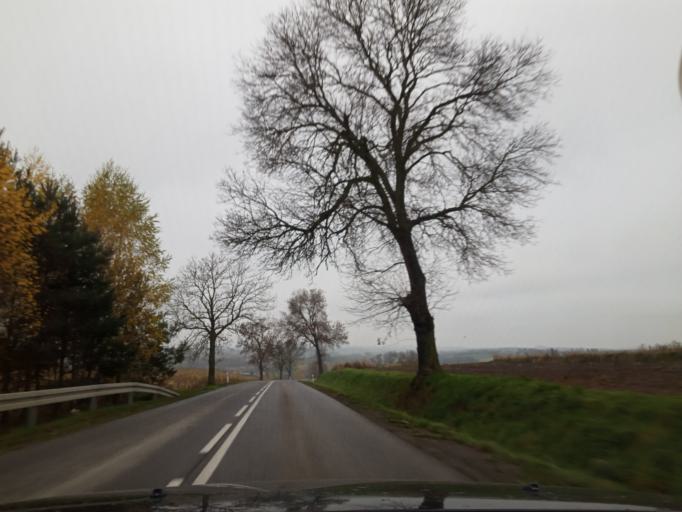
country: PL
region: Swietokrzyskie
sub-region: Powiat pinczowski
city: Dzialoszyce
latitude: 50.3572
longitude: 20.3618
